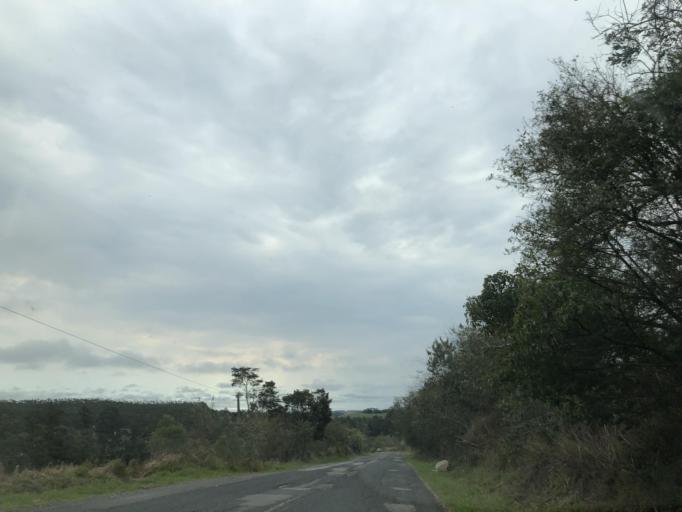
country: BR
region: Sao Paulo
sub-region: Pilar Do Sul
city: Pilar do Sul
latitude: -23.8143
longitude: -47.6371
